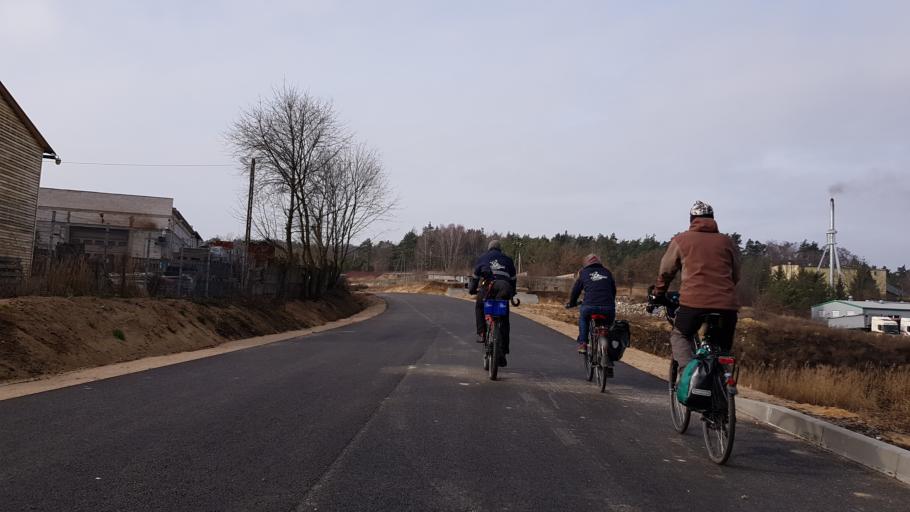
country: PL
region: West Pomeranian Voivodeship
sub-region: Powiat mysliborski
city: Barlinek
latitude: 53.0037
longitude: 15.2258
